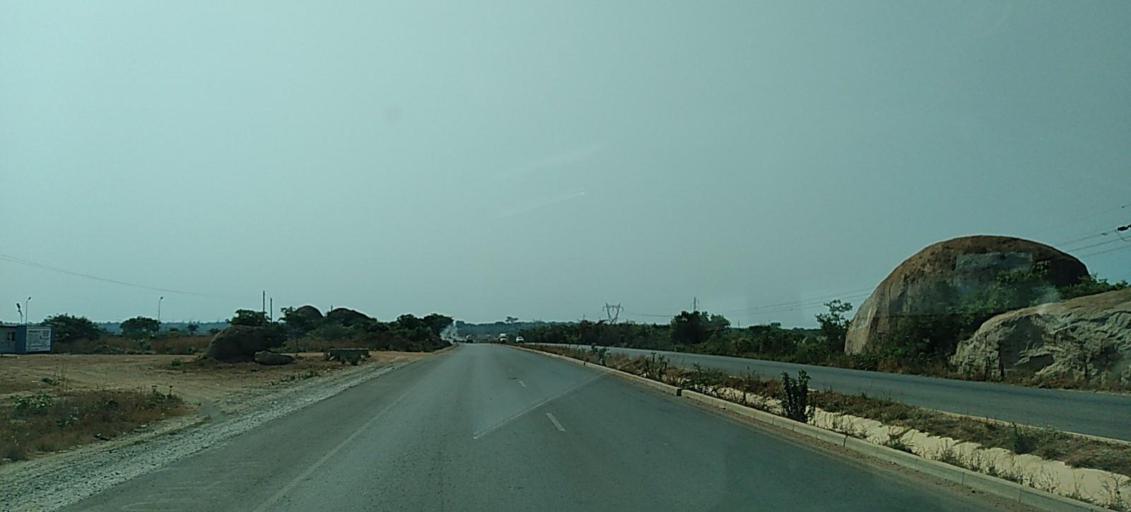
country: ZM
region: Copperbelt
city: Chingola
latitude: -12.5719
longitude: 27.9114
